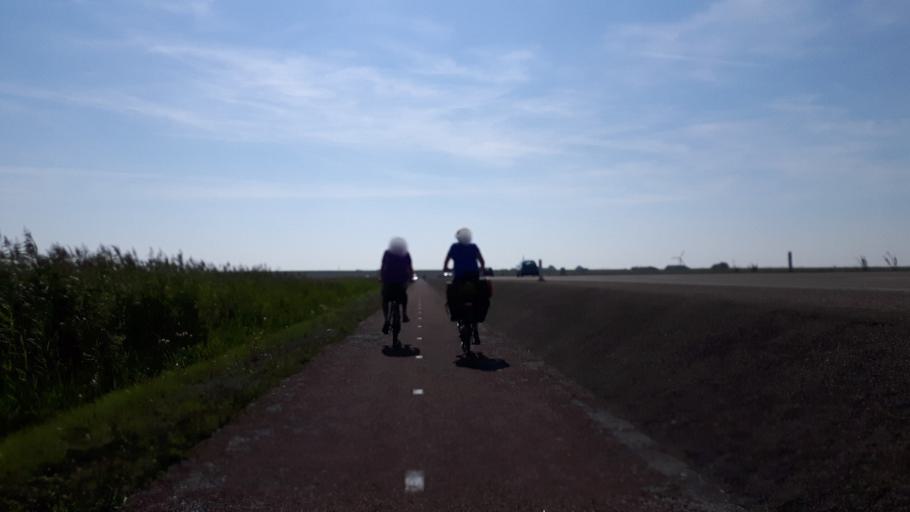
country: NL
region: Friesland
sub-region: Gemeente Dongeradeel
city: Holwerd
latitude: 53.3849
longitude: 5.8892
